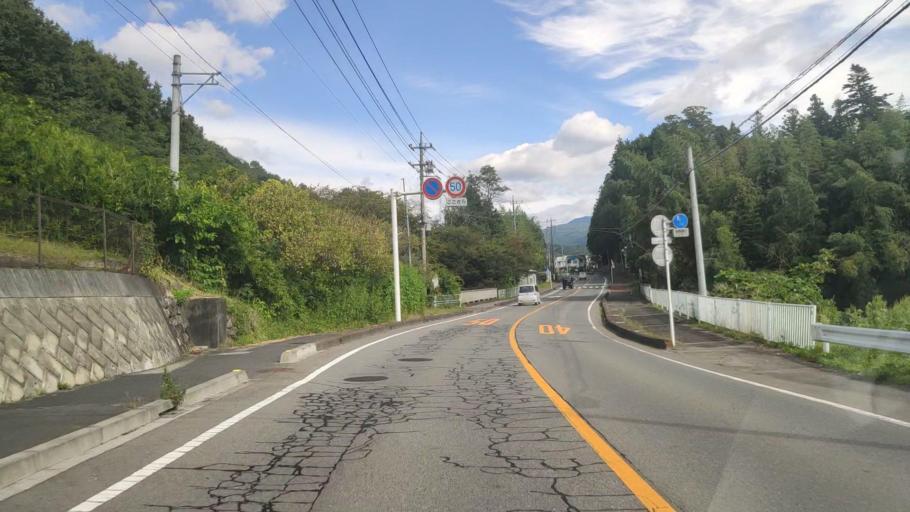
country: JP
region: Gunma
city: Nakanojomachi
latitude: 36.5904
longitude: 138.8605
